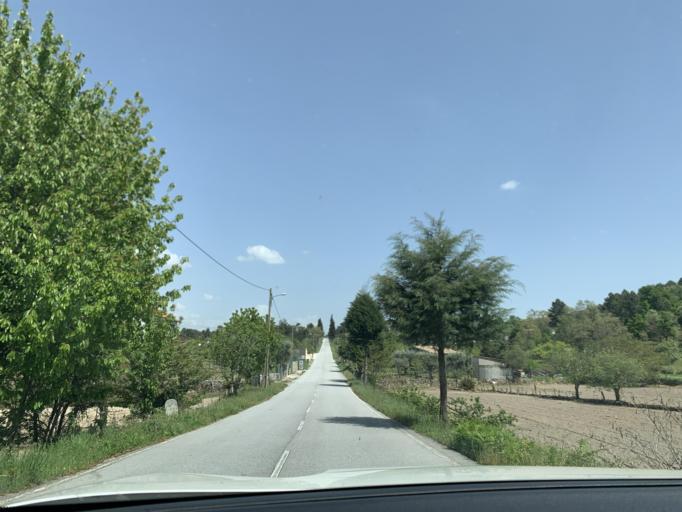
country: PT
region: Guarda
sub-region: Fornos de Algodres
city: Fornos de Algodres
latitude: 40.5808
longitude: -7.6324
